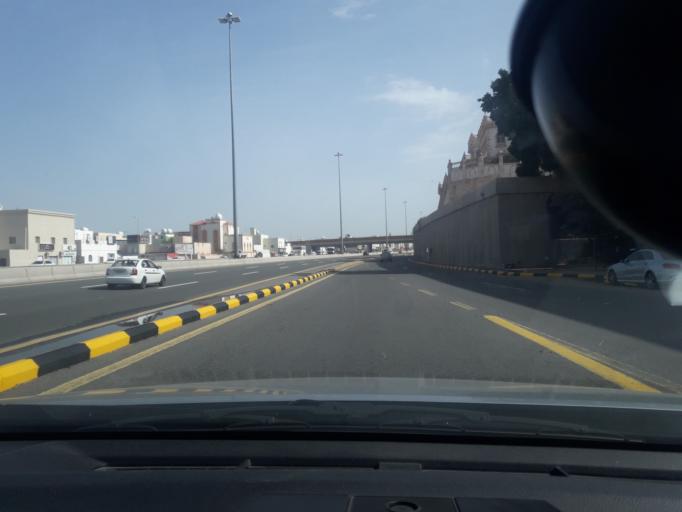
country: SA
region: Al Madinah al Munawwarah
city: Medina
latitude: 24.4472
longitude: 39.6563
